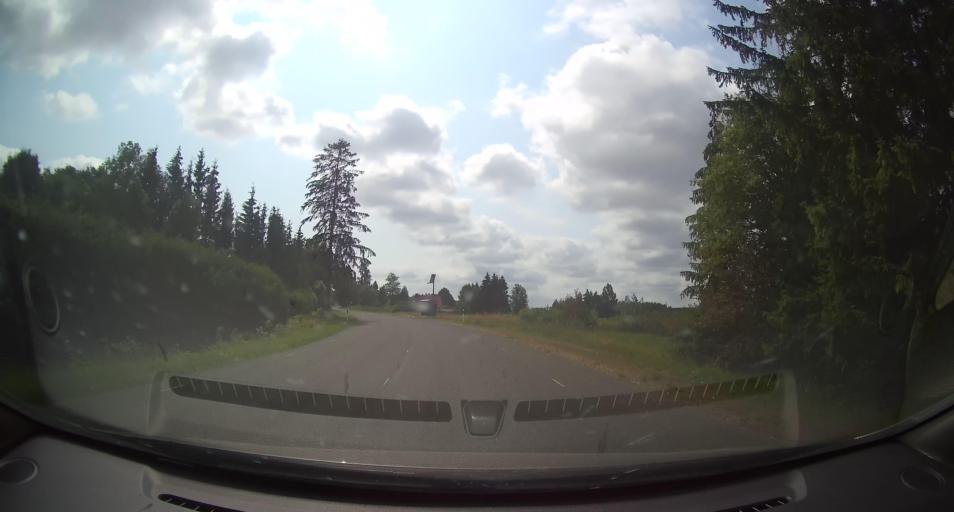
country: EE
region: Paernumaa
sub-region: Audru vald
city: Audru
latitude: 58.4964
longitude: 24.3364
